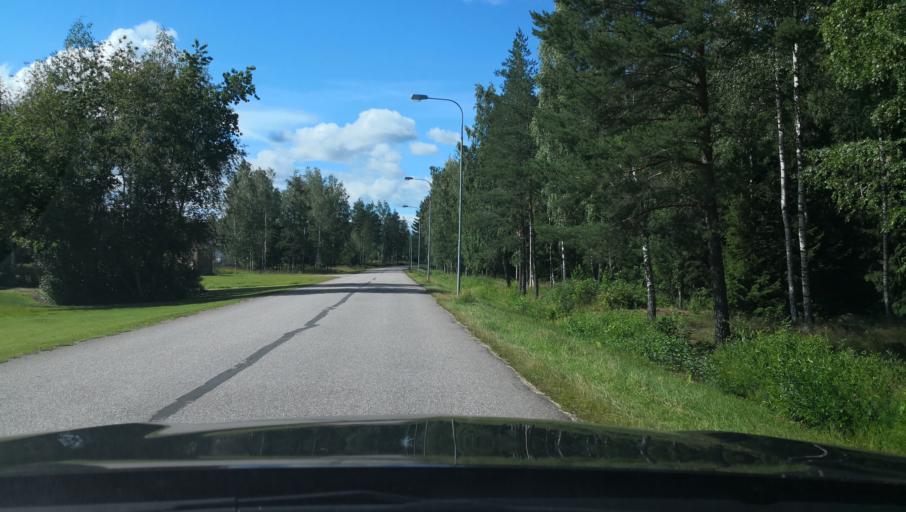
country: SE
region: Vaestmanland
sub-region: Surahammars Kommun
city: Surahammar
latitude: 59.6946
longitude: 16.2439
